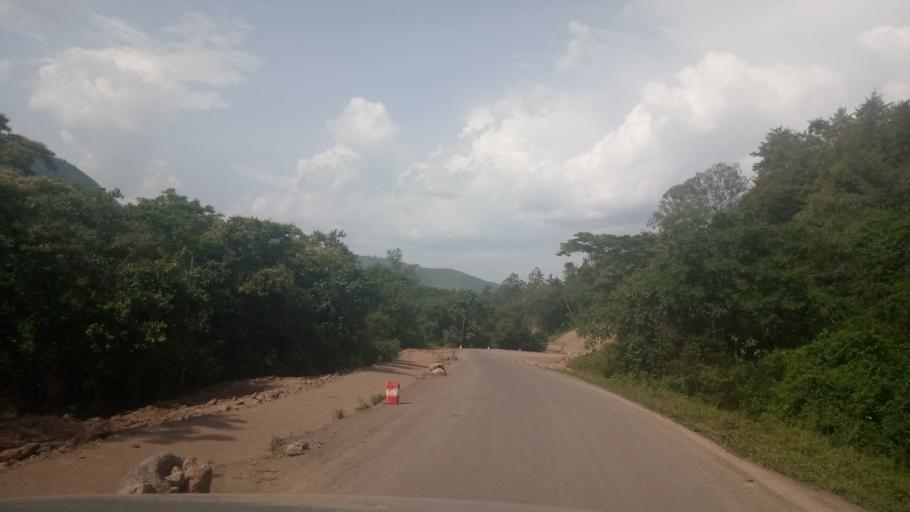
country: ET
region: Oromiya
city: Agaro
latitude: 8.0425
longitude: 36.4703
